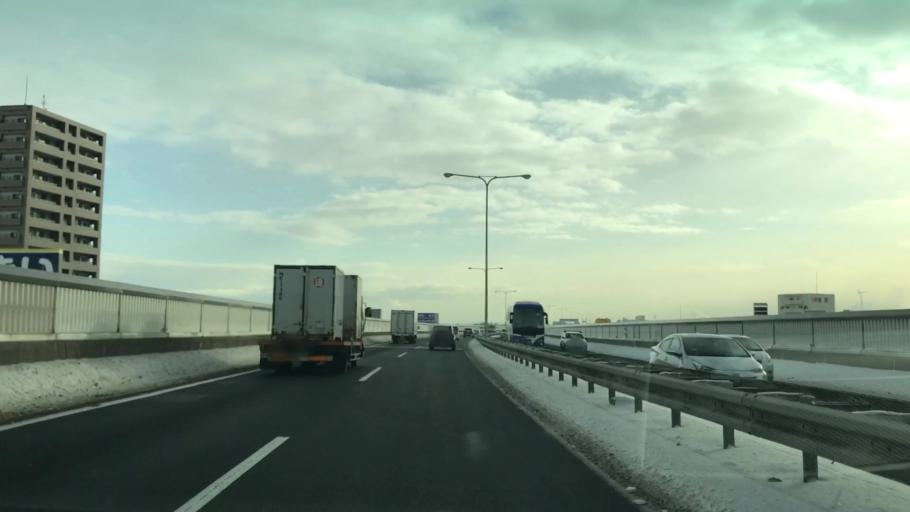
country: JP
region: Hokkaido
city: Sapporo
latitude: 43.1041
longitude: 141.3765
